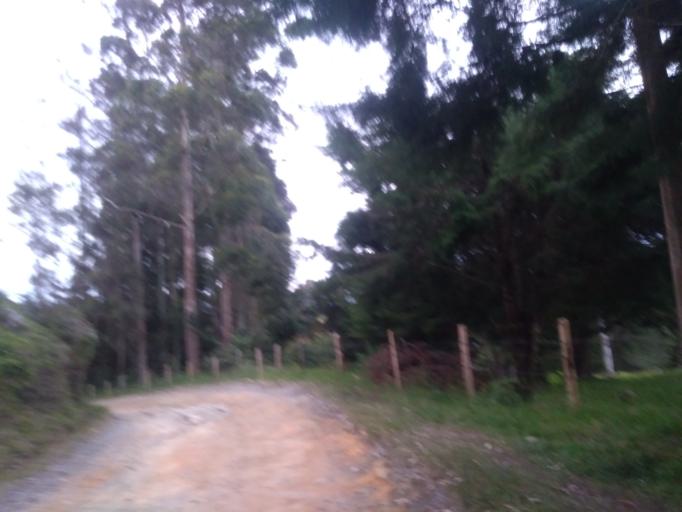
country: CO
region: Antioquia
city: Bello
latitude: 6.3547
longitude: -75.6090
